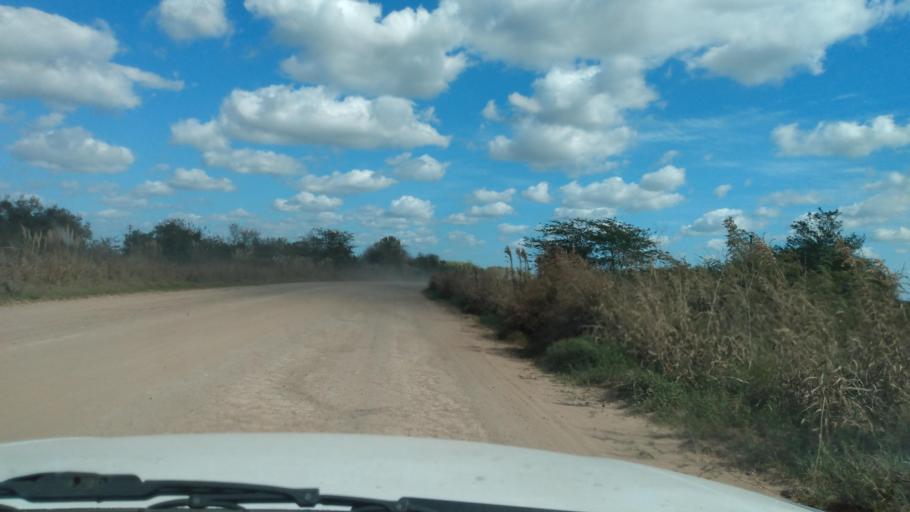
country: AR
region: Buenos Aires
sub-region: Partido de Navarro
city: Navarro
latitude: -34.9976
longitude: -59.3188
